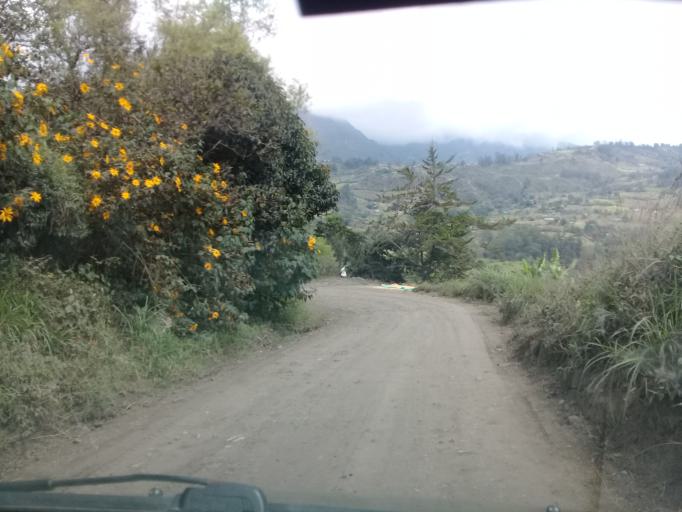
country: CO
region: Cundinamarca
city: Caqueza
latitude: 4.4140
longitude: -73.9831
